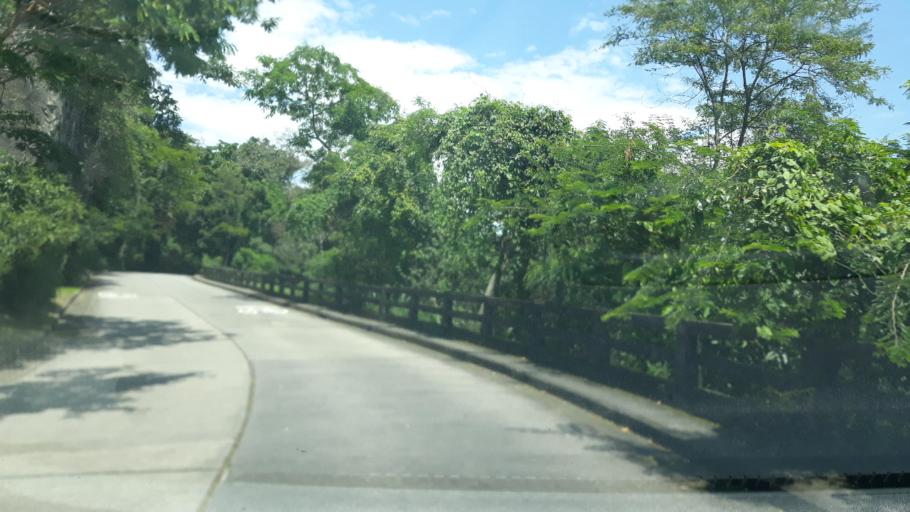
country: BR
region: Rio de Janeiro
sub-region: Rio De Janeiro
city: Rio de Janeiro
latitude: -22.9482
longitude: -43.2065
